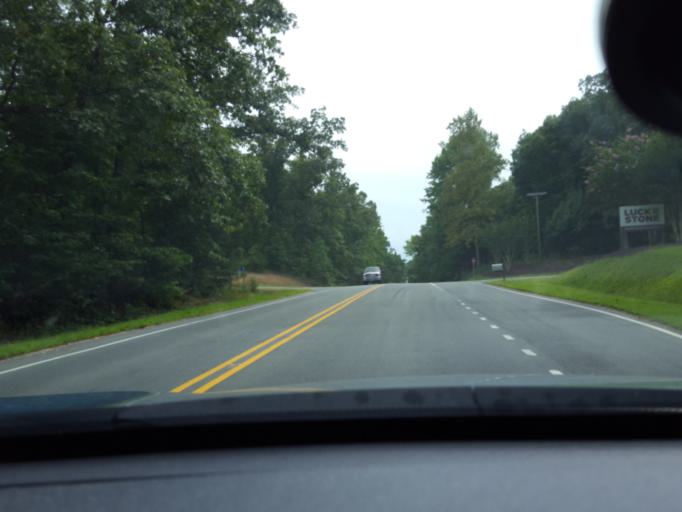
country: US
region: Virginia
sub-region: Caroline County
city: Bowling Green
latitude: 37.9948
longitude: -77.3364
